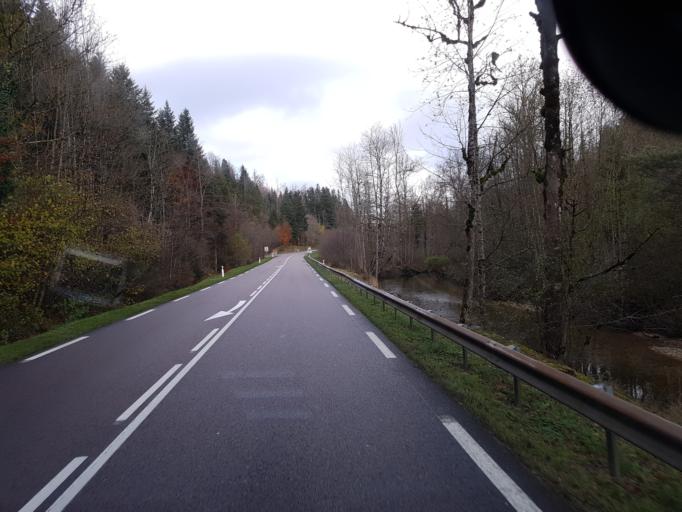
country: FR
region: Franche-Comte
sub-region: Departement du Jura
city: Champagnole
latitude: 46.6451
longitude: 5.9402
